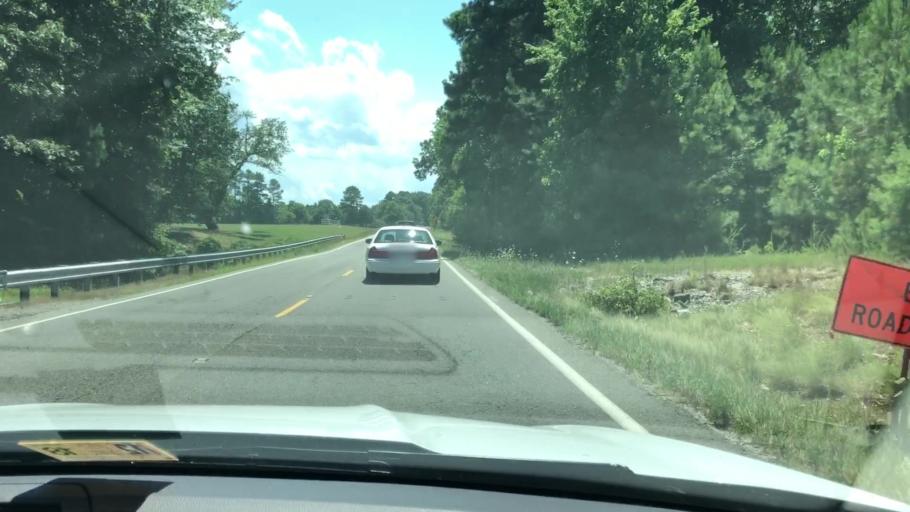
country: US
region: Virginia
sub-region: Middlesex County
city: Deltaville
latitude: 37.6030
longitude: -76.4410
